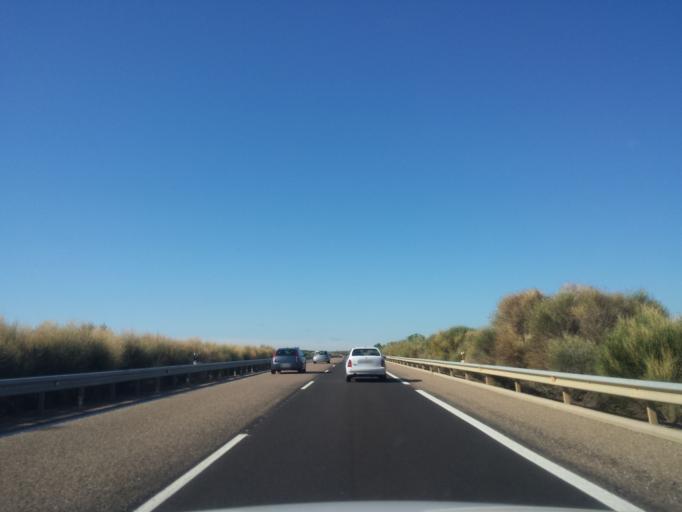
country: ES
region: Castille and Leon
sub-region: Provincia de Zamora
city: San Cristobal de Entrevinas
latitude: 42.0726
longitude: -5.6601
